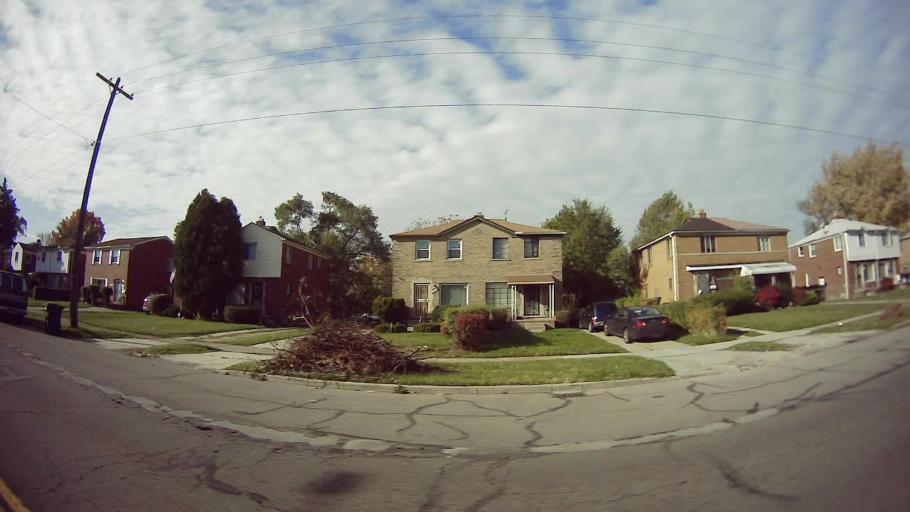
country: US
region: Michigan
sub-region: Oakland County
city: Oak Park
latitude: 42.4315
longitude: -83.1805
